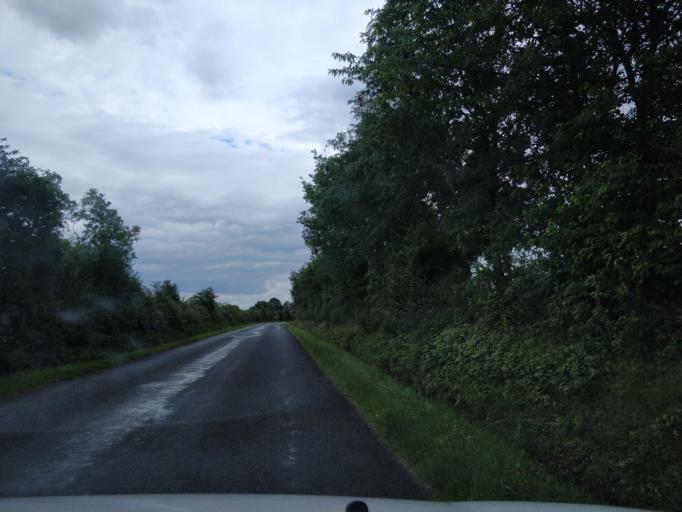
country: FR
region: Pays de la Loire
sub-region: Departement de Maine-et-Loire
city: Grez-Neuville
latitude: 47.6332
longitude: -0.6300
